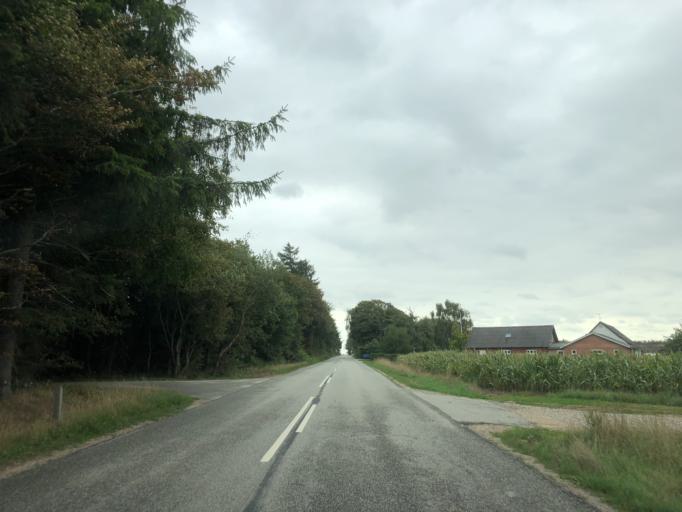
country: DK
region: Central Jutland
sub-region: Herning Kommune
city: Vildbjerg
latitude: 56.1840
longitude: 8.8279
